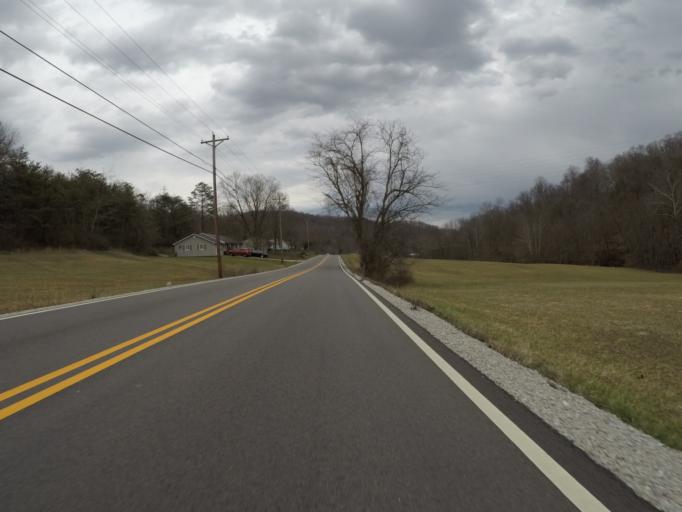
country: US
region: Ohio
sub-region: Lawrence County
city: Burlington
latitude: 38.4484
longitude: -82.5101
